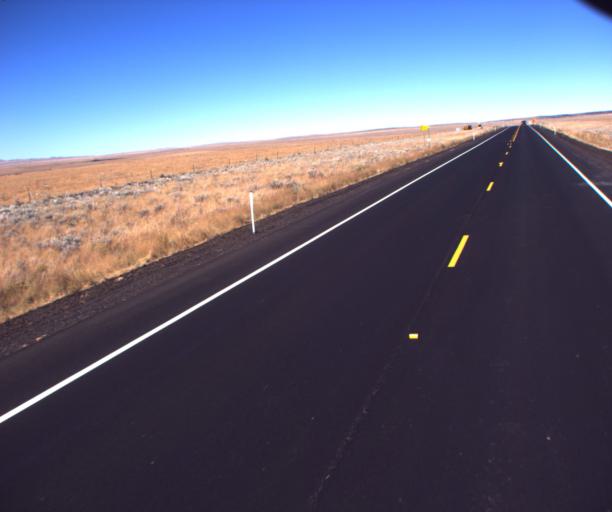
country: US
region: Arizona
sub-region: Apache County
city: Springerville
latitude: 34.2666
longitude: -109.3594
